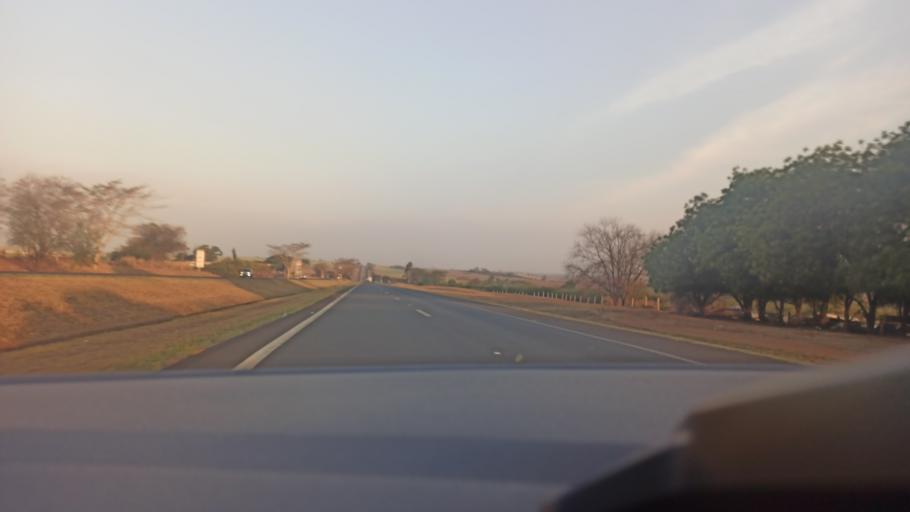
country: BR
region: Sao Paulo
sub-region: Santa Adelia
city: Santa Adelia
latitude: -21.3630
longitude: -48.7611
